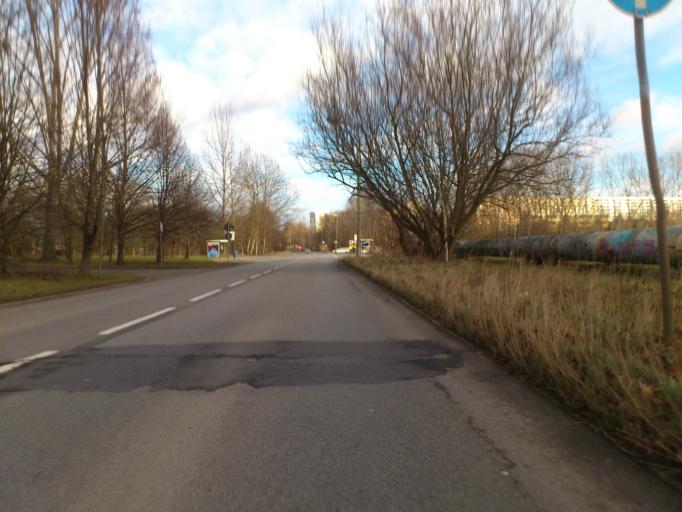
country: DE
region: Saxony
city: Neukirchen
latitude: 50.7857
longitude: 12.8895
